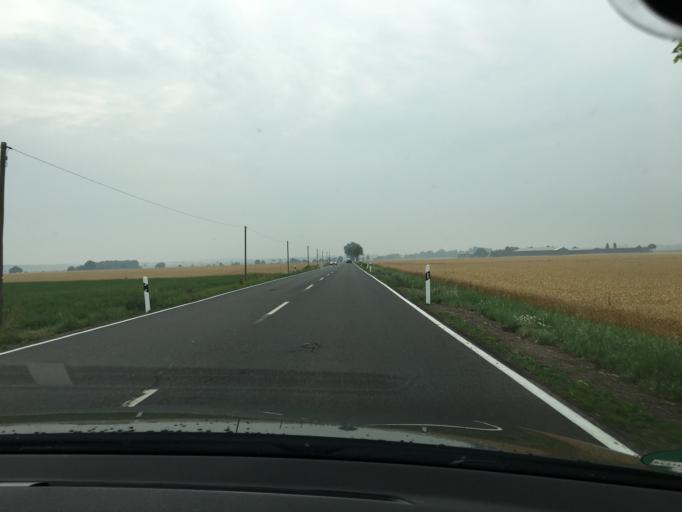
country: DE
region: North Rhine-Westphalia
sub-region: Regierungsbezirk Koln
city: Titz
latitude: 50.9825
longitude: 6.4014
